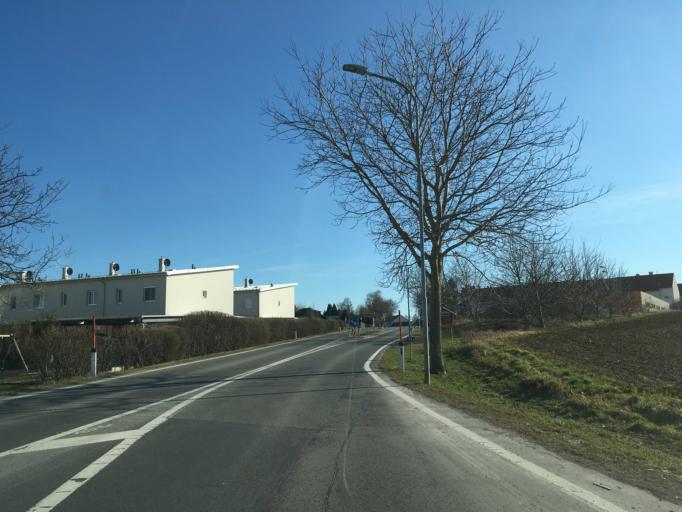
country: AT
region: Burgenland
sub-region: Eisenstadt-Umgebung
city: Hornstein
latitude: 47.8881
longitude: 16.4388
